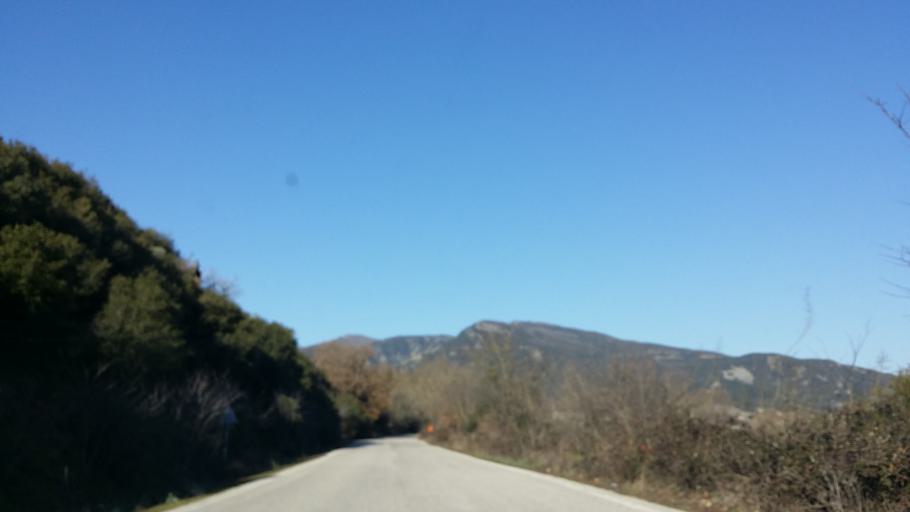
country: GR
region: West Greece
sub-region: Nomos Aitolias kai Akarnanias
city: Sardinia
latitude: 38.8610
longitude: 21.3393
